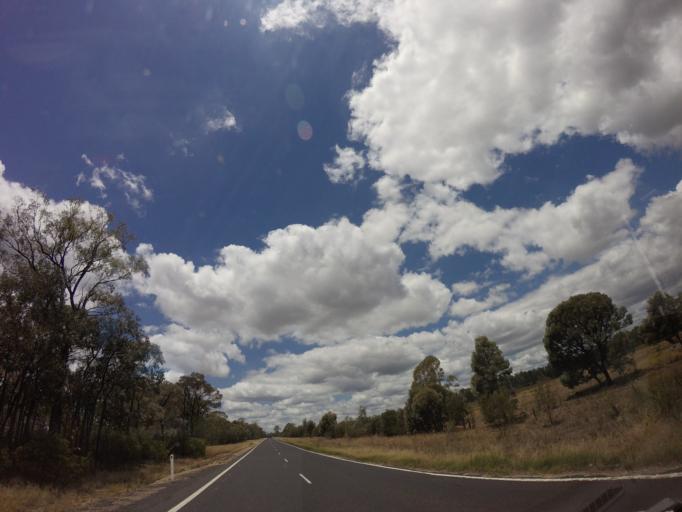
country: AU
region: Queensland
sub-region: Goondiwindi
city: Goondiwindi
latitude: -28.0332
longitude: 150.8217
